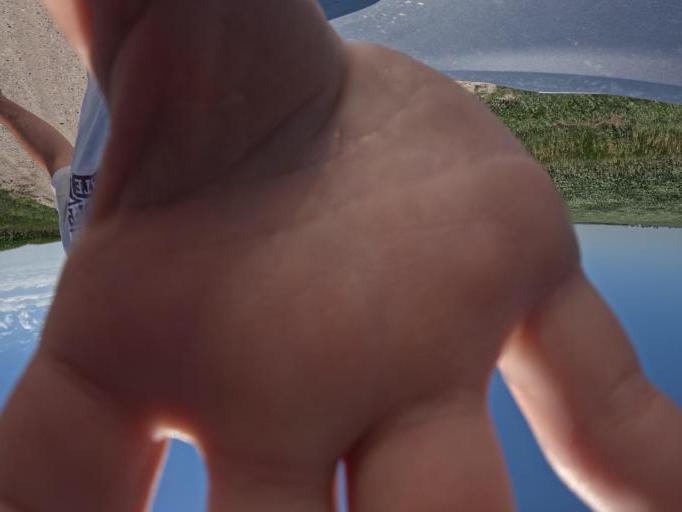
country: US
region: Iowa
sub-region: Keokuk County
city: Sigourney
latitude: 41.4495
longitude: -92.3357
